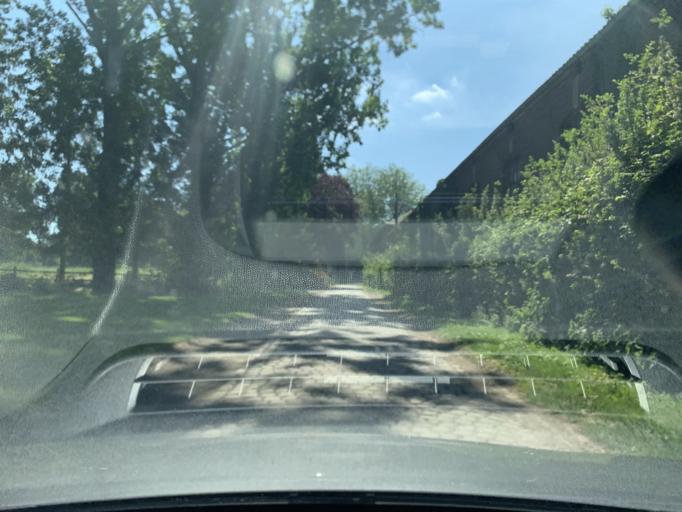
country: FR
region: Nord-Pas-de-Calais
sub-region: Departement du Nord
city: Caudry
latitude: 50.1004
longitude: 3.4179
